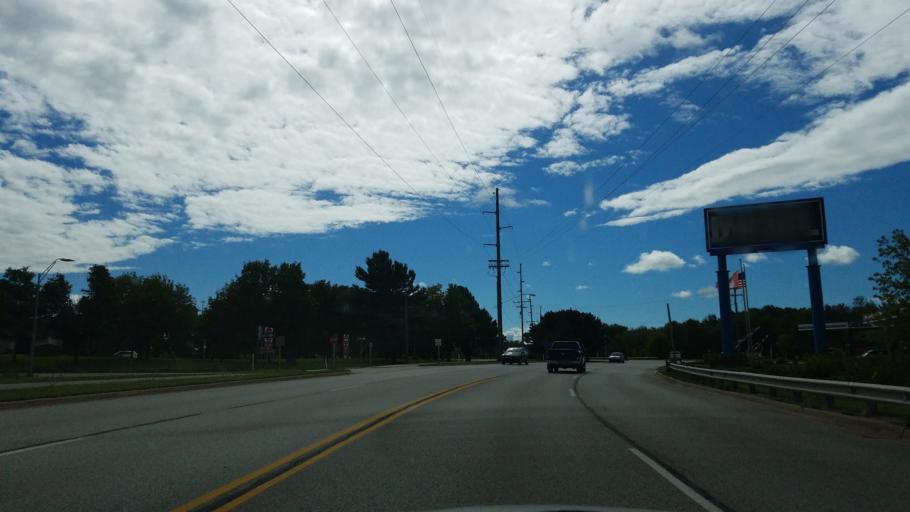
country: US
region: Michigan
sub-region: Chippewa County
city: Sault Ste. Marie
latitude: 46.4938
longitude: -84.3707
